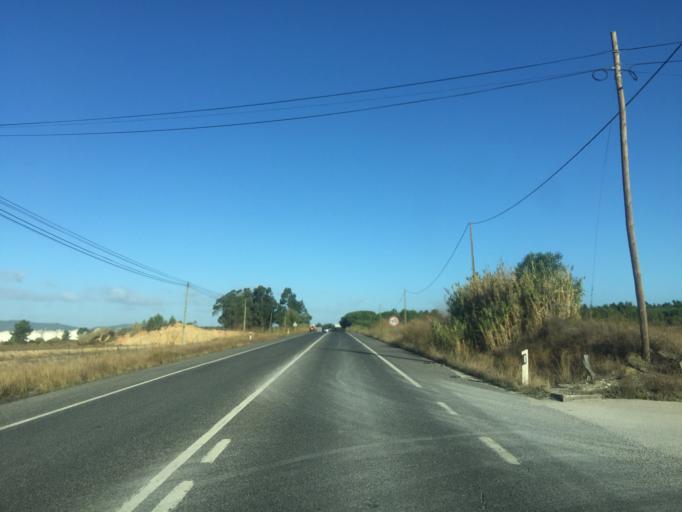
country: PT
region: Lisbon
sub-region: Azambuja
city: Aveiras de Cima
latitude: 39.1660
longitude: -8.9204
